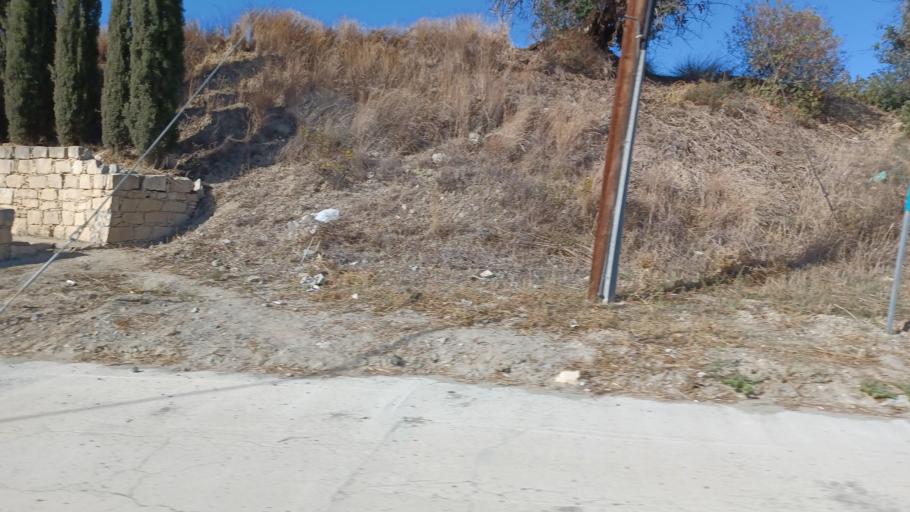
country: CY
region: Limassol
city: Pyrgos
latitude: 34.7495
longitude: 33.2165
